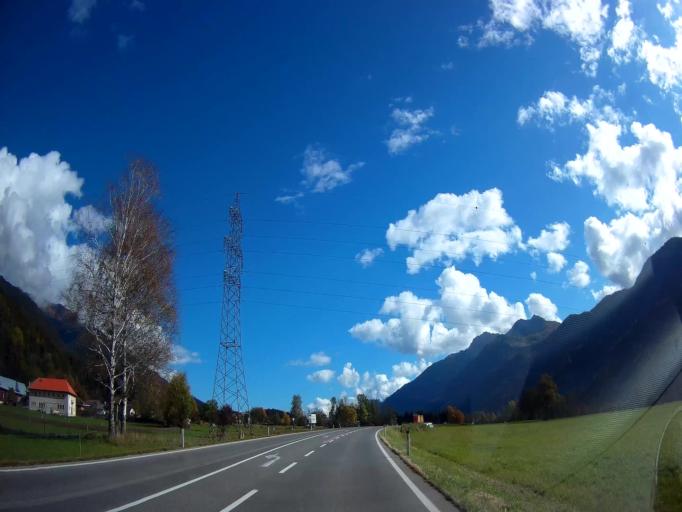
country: AT
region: Carinthia
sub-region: Politischer Bezirk Spittal an der Drau
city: Oberdrauburg
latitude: 46.7499
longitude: 12.9874
